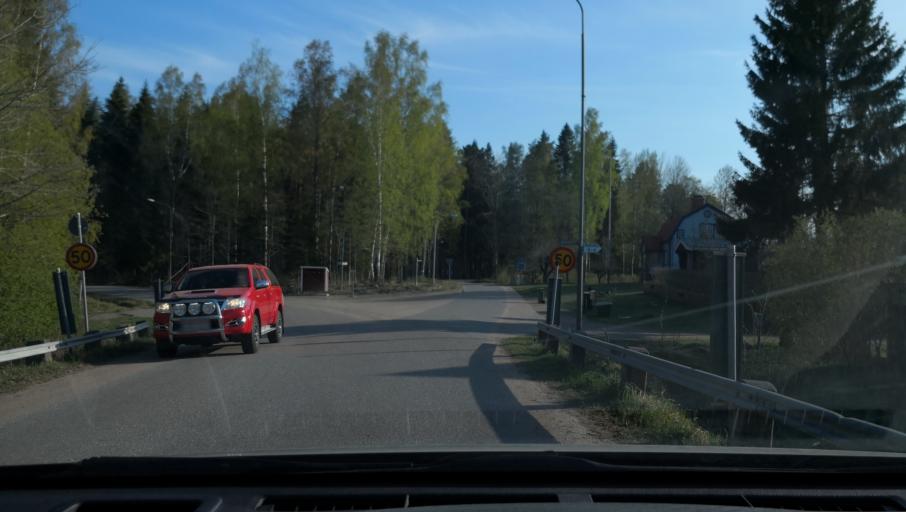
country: SE
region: Uppsala
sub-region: Heby Kommun
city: Tarnsjo
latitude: 60.2838
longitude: 16.8831
